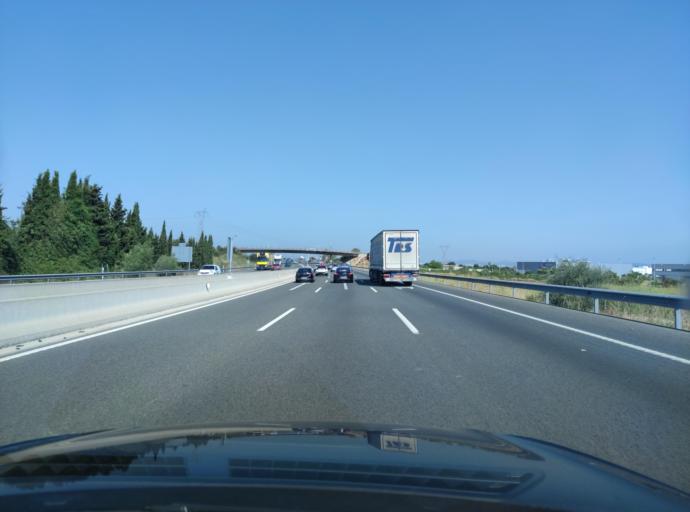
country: ES
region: Valencia
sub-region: Provincia de Valencia
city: Torrent
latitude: 39.4138
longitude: -0.5032
